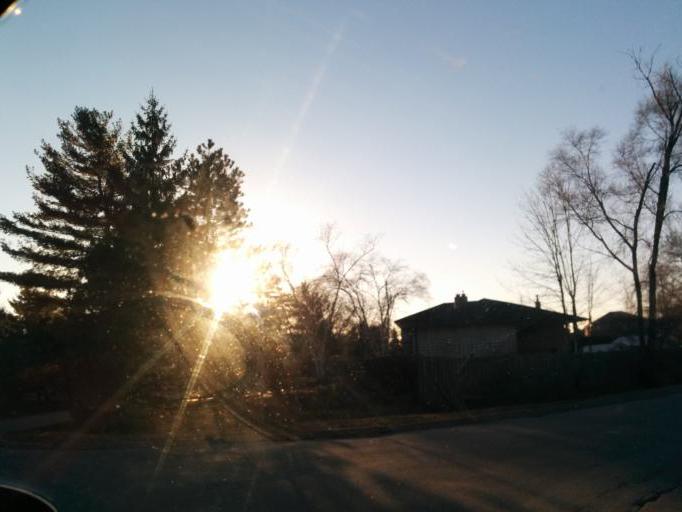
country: CA
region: Ontario
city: Mississauga
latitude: 43.5603
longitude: -79.6214
